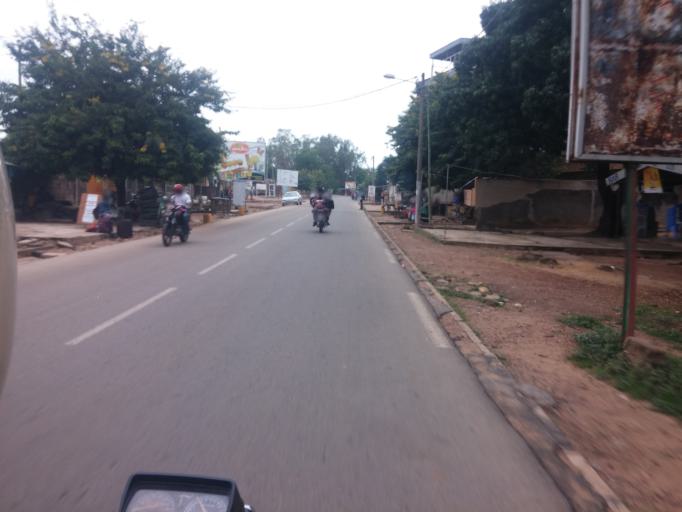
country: TG
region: Kara
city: Kara
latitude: 9.5492
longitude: 1.1864
